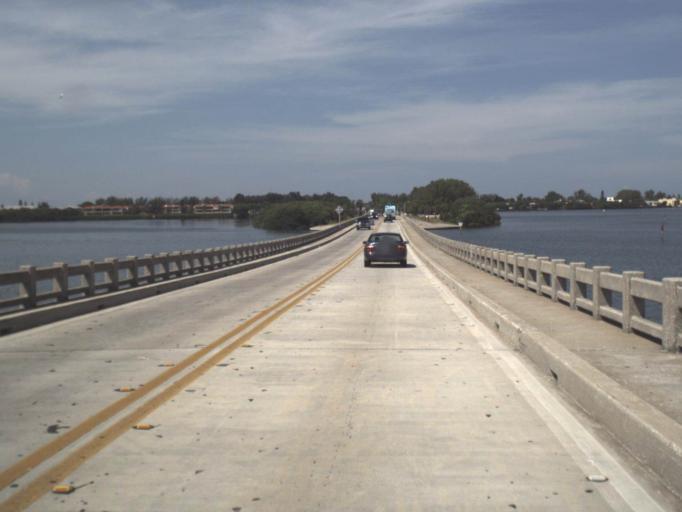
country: US
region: Florida
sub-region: Manatee County
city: Holmes Beach
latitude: 27.4968
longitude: -82.6964
